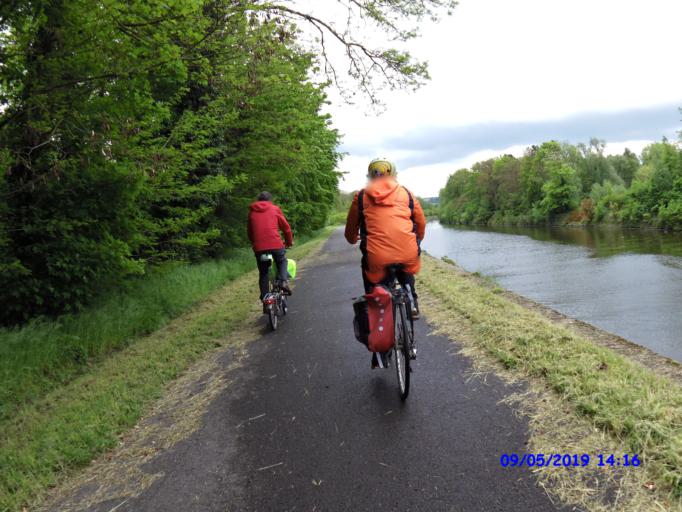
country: BE
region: Wallonia
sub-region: Province du Hainaut
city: Aiseau
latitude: 50.4340
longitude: 4.5873
